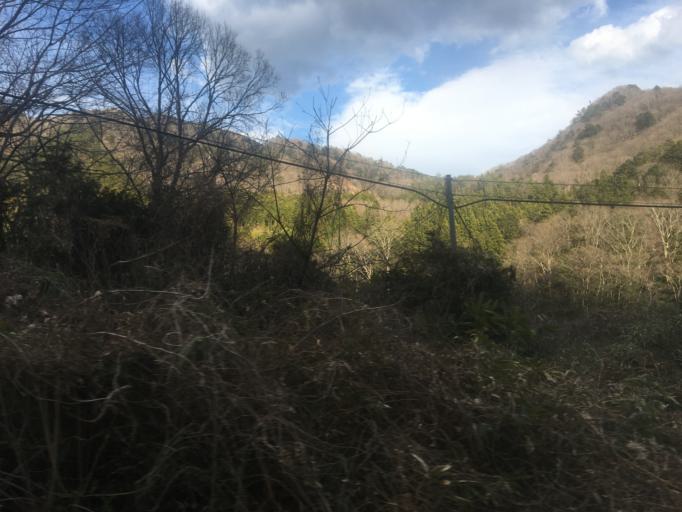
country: JP
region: Fukushima
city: Iwaki
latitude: 37.1760
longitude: 140.8291
